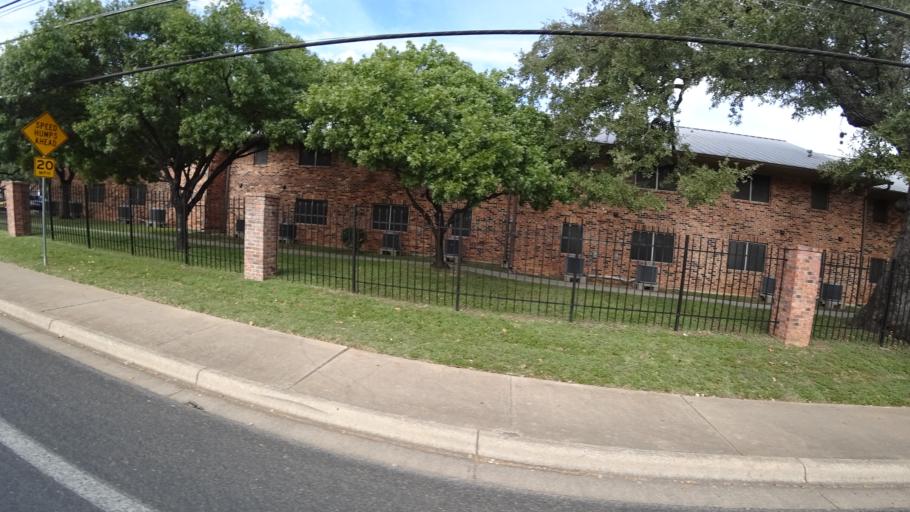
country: US
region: Texas
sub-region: Travis County
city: Austin
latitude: 30.2186
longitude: -97.7677
